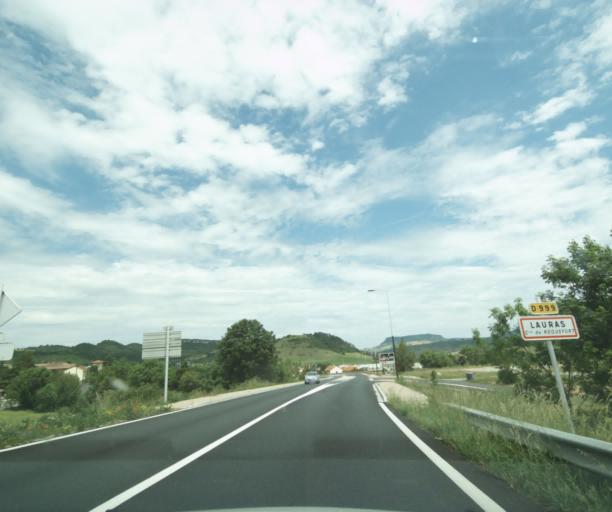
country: FR
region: Midi-Pyrenees
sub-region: Departement de l'Aveyron
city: Saint-Affrique
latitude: 43.9704
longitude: 2.9614
